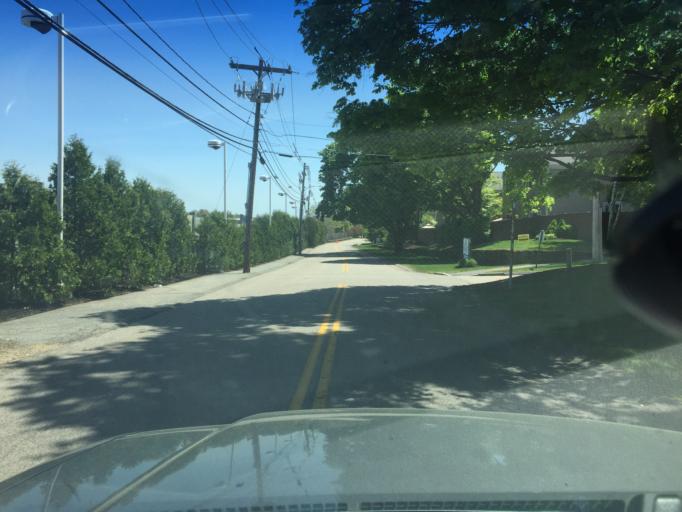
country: US
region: Massachusetts
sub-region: Norfolk County
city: Norwood
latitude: 42.1964
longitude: -71.1868
